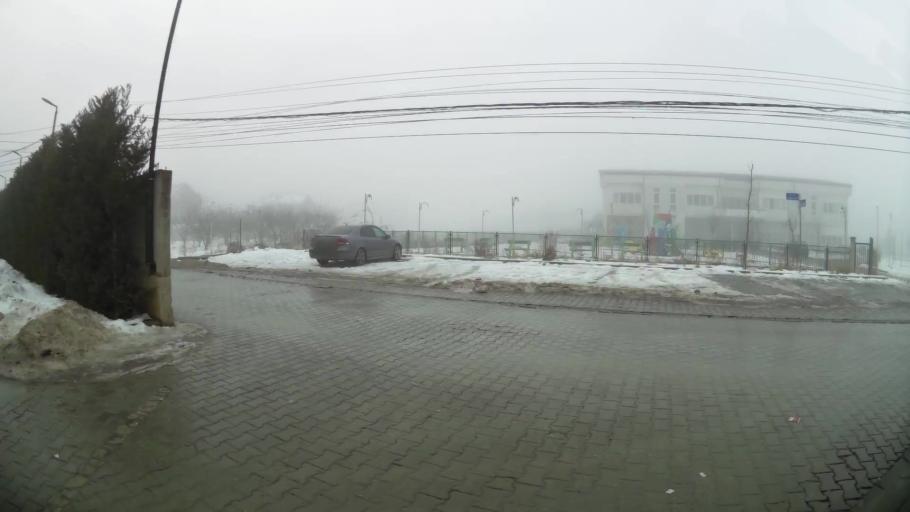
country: XK
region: Pristina
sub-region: Komuna e Prishtines
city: Pristina
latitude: 42.6421
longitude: 21.1441
